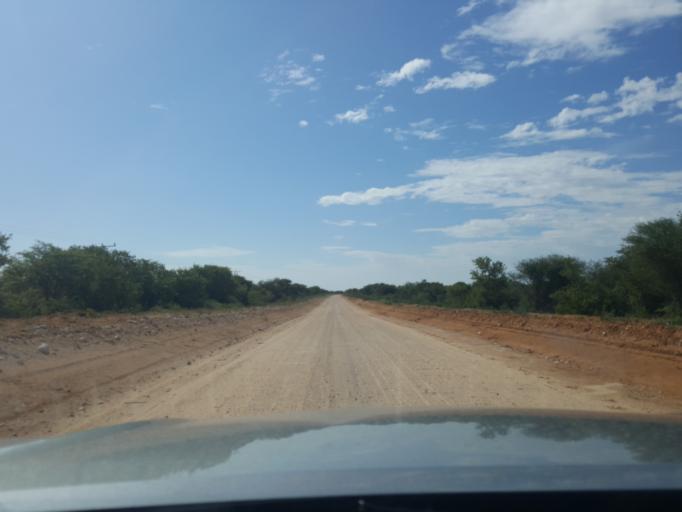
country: BW
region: Kweneng
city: Khudumelapye
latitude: -23.7687
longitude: 24.7654
